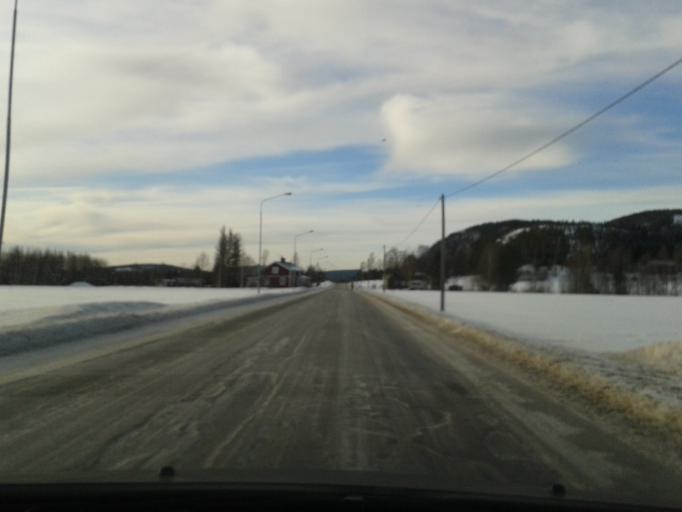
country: SE
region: Vaesternorrland
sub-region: OErnskoeldsviks Kommun
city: Bredbyn
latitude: 63.5263
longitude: 18.0349
